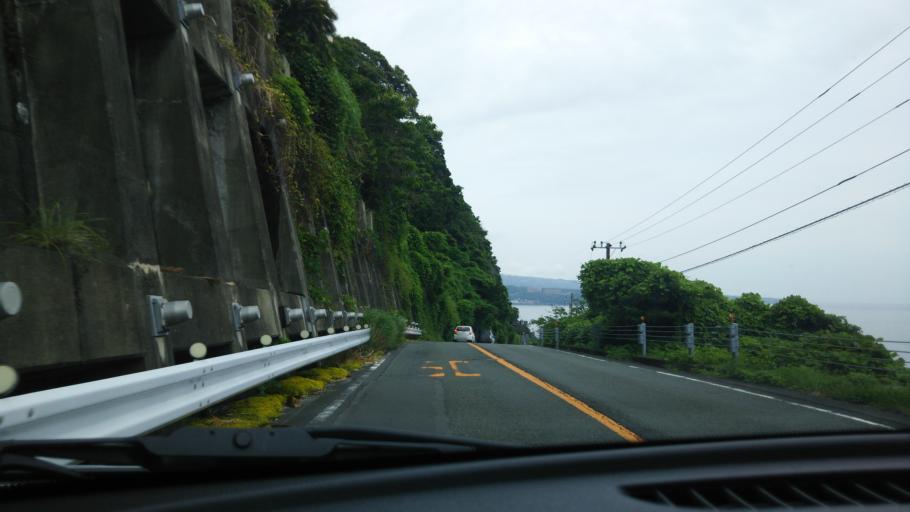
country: JP
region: Shizuoka
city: Ito
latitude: 34.8326
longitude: 139.0749
